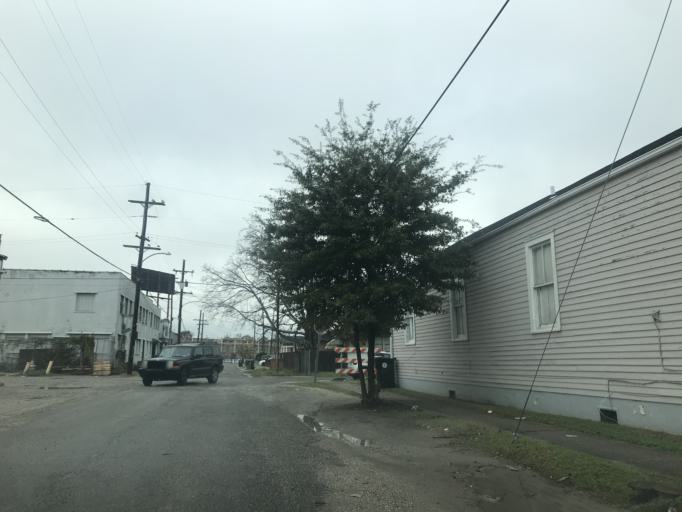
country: US
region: Louisiana
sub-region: Orleans Parish
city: New Orleans
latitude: 29.9737
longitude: -90.1095
